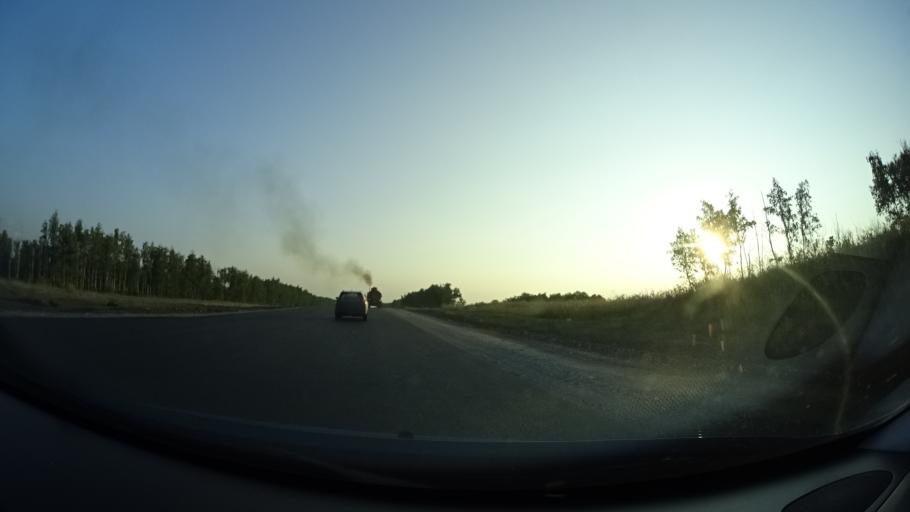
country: RU
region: Samara
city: Isakly
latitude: 53.9931
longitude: 51.5302
